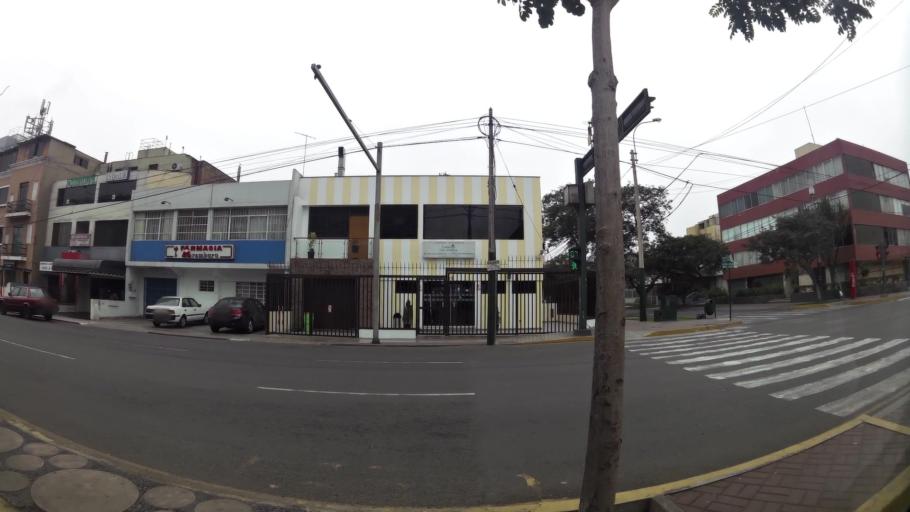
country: PE
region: Lima
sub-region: Lima
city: San Isidro
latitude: -12.1032
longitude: -77.0296
